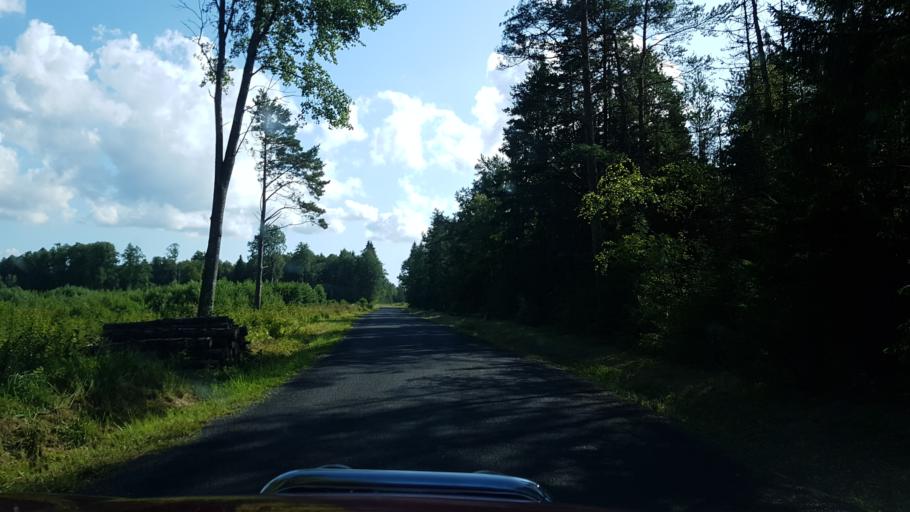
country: EE
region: Harju
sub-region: Paldiski linn
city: Paldiski
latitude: 59.2735
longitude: 24.0278
